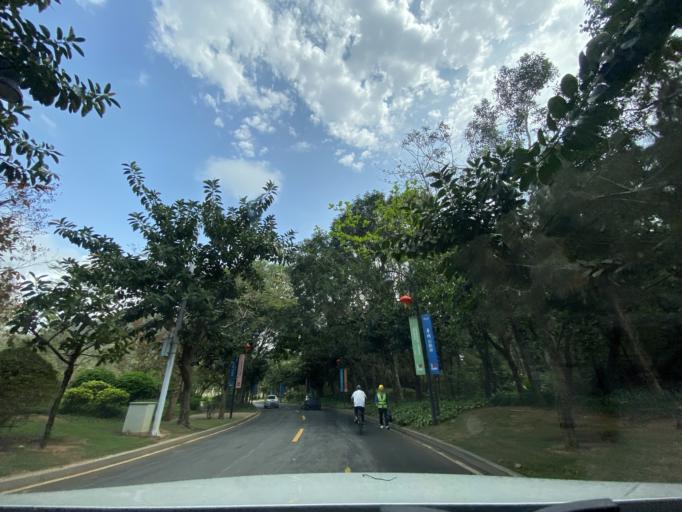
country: CN
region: Hainan
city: Liji
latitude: 18.6689
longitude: 110.2632
